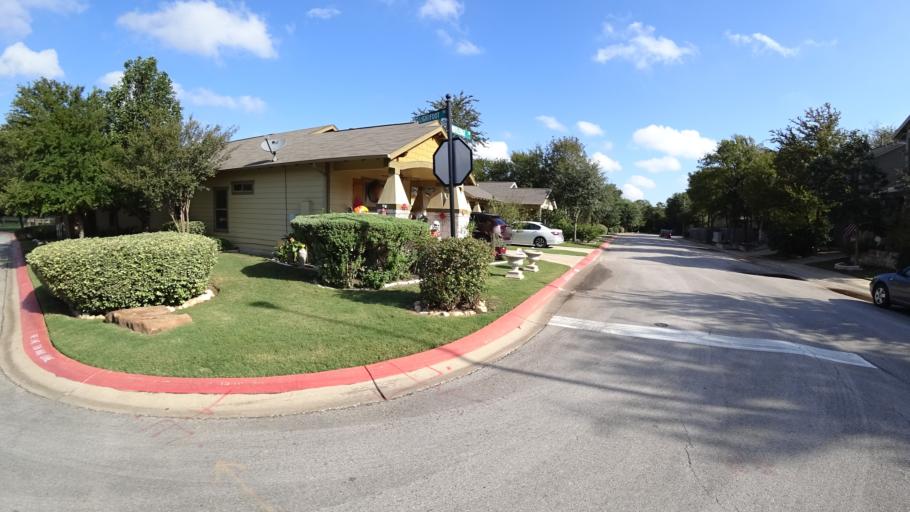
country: US
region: Texas
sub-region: Travis County
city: Rollingwood
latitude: 30.2146
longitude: -97.8082
